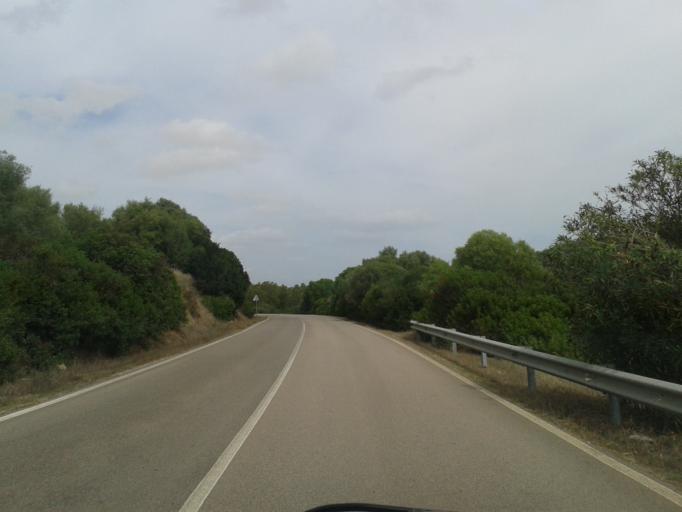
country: IT
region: Sardinia
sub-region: Provincia di Cagliari
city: Villasimius
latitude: 39.1777
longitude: 9.5637
